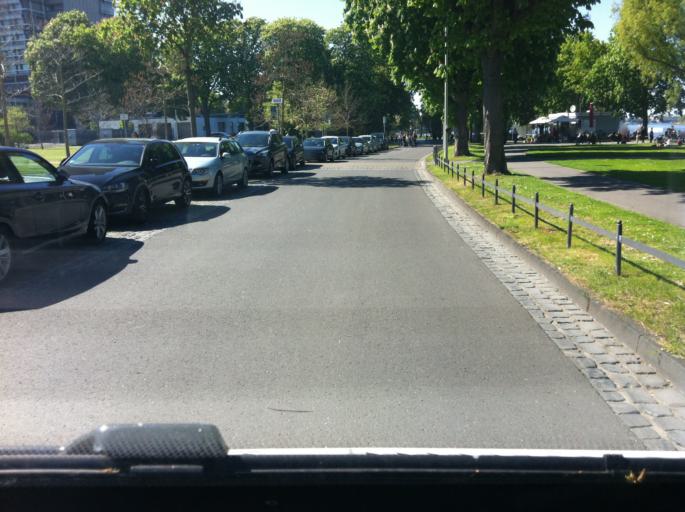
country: DE
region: North Rhine-Westphalia
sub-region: Regierungsbezirk Koln
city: Bonn
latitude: 50.7183
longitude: 7.1303
